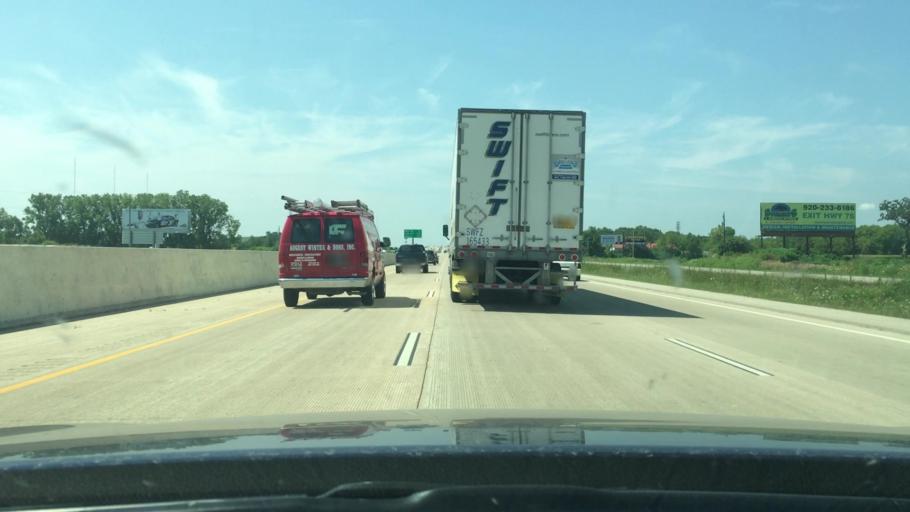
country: US
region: Wisconsin
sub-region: Winnebago County
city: Oshkosh
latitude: 44.1060
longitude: -88.5303
